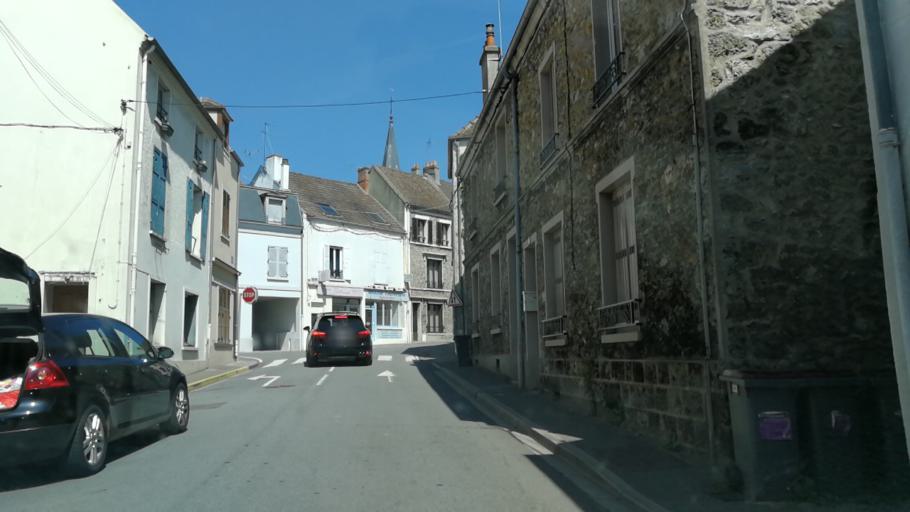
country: FR
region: Ile-de-France
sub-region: Departement des Yvelines
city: Chevreuse
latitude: 48.7072
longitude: 2.0392
